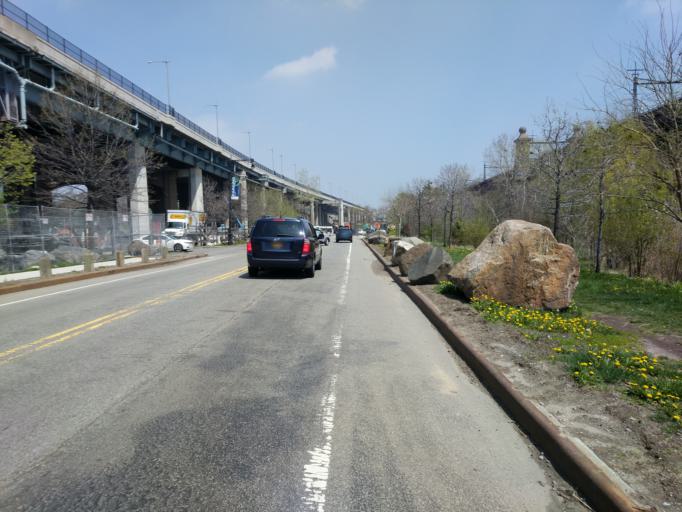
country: US
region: New York
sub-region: New York County
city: Manhattan
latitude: 40.7916
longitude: -73.9244
